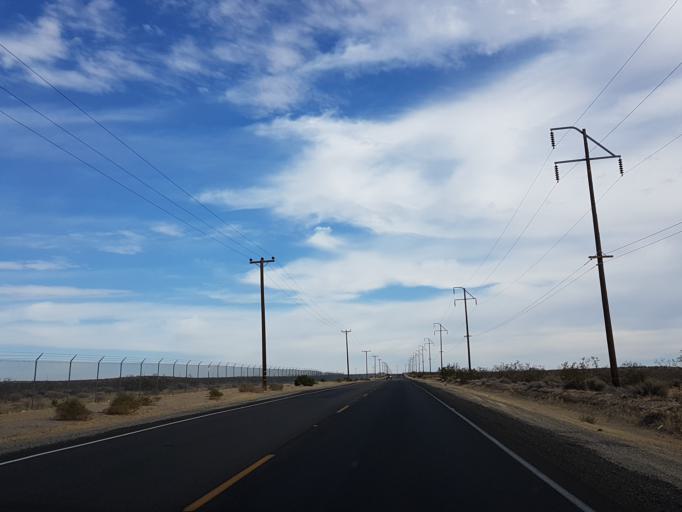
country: US
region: California
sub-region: Kern County
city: Ridgecrest
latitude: 35.6226
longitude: -117.6116
